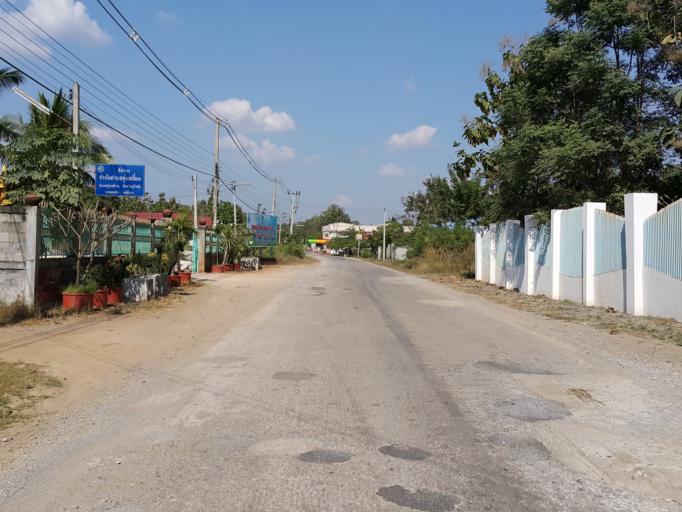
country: TH
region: Sukhothai
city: Thung Saliam
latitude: 17.3315
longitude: 99.5501
